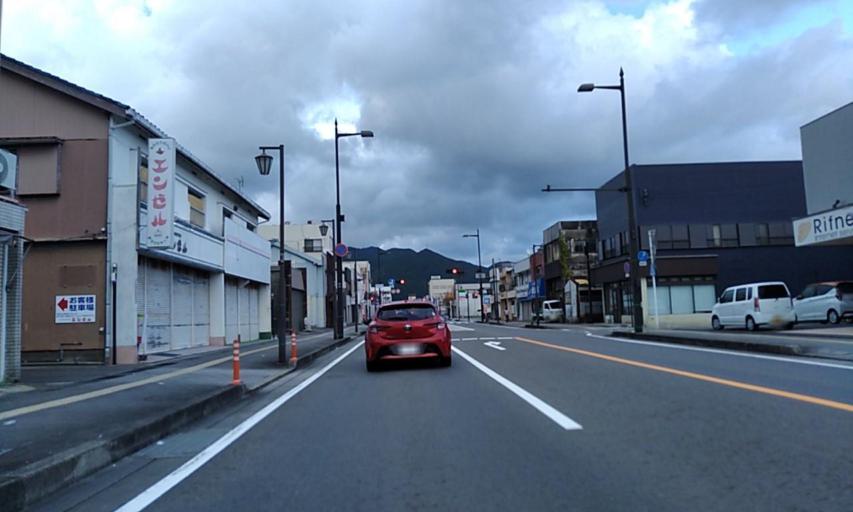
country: JP
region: Wakayama
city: Shingu
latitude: 33.7236
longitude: 135.9865
